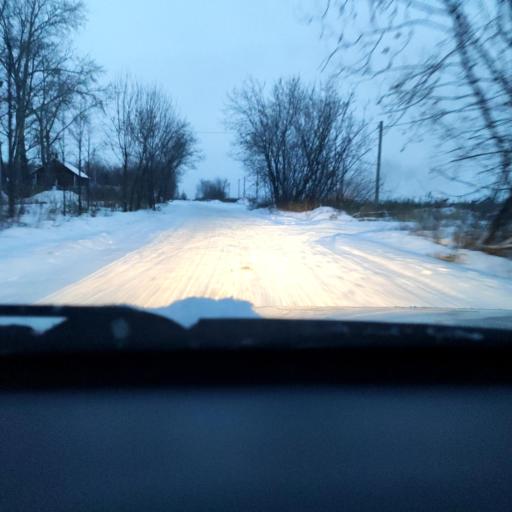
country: RU
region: Perm
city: Froly
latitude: 57.9490
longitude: 56.2319
